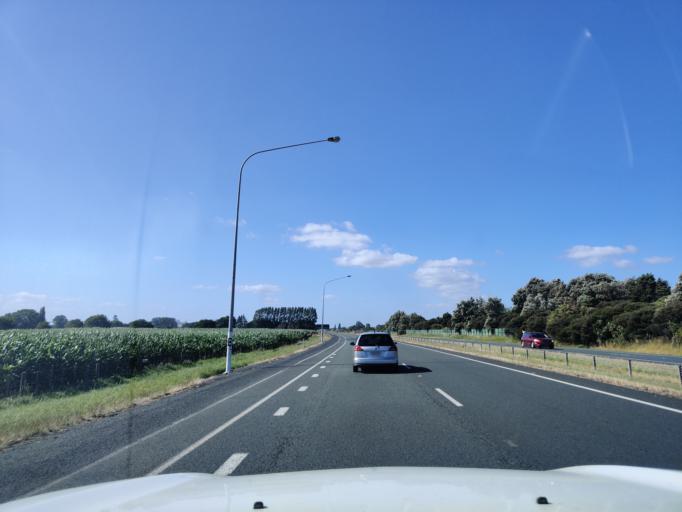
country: NZ
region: Waikato
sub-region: Waikato District
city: Te Kauwhata
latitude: -37.4849
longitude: 175.1603
